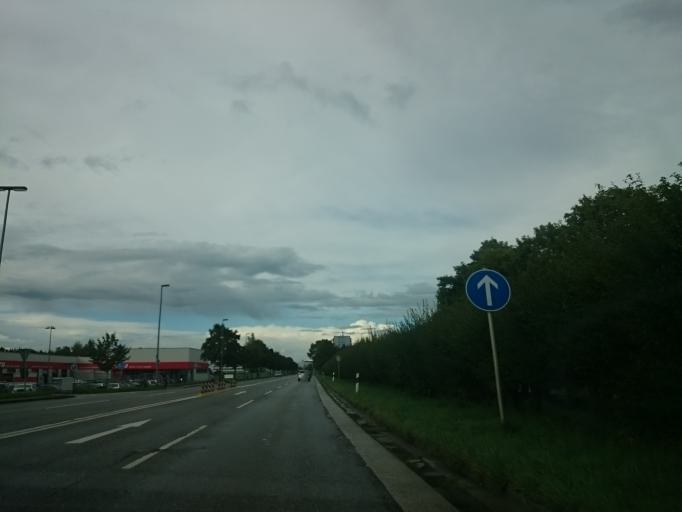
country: DE
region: Bavaria
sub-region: Swabia
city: Kempten (Allgaeu)
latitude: 47.7373
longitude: 10.3235
